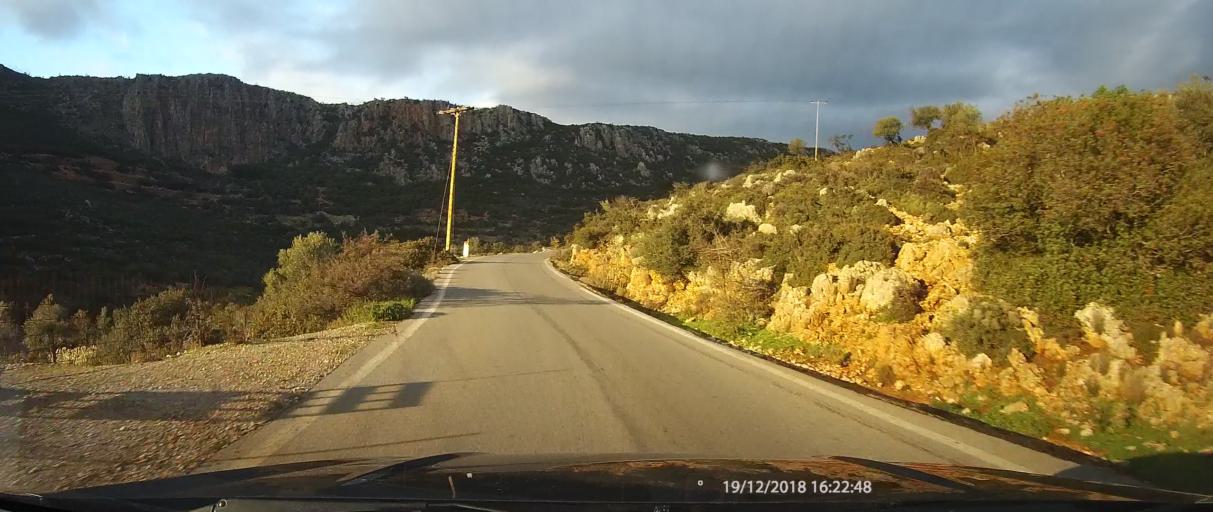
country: GR
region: Peloponnese
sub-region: Nomos Lakonias
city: Kato Glikovrisi
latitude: 36.9452
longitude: 22.8315
